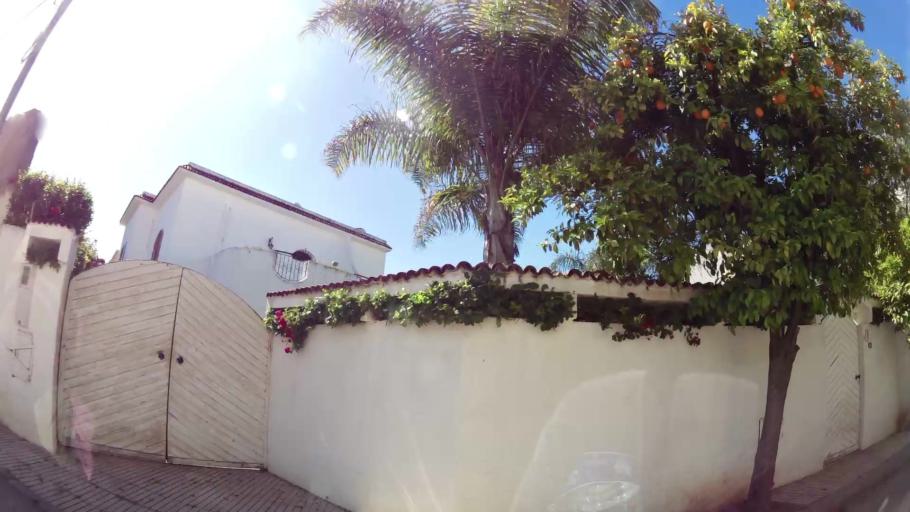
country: MA
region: Fes-Boulemane
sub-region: Fes
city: Fes
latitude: 34.0203
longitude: -4.9954
